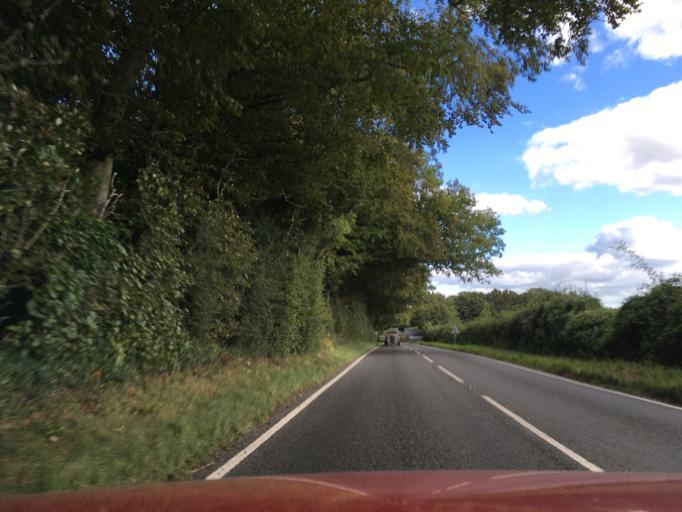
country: GB
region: England
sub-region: Hampshire
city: Chandlers Ford
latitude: 51.1036
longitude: -1.4128
